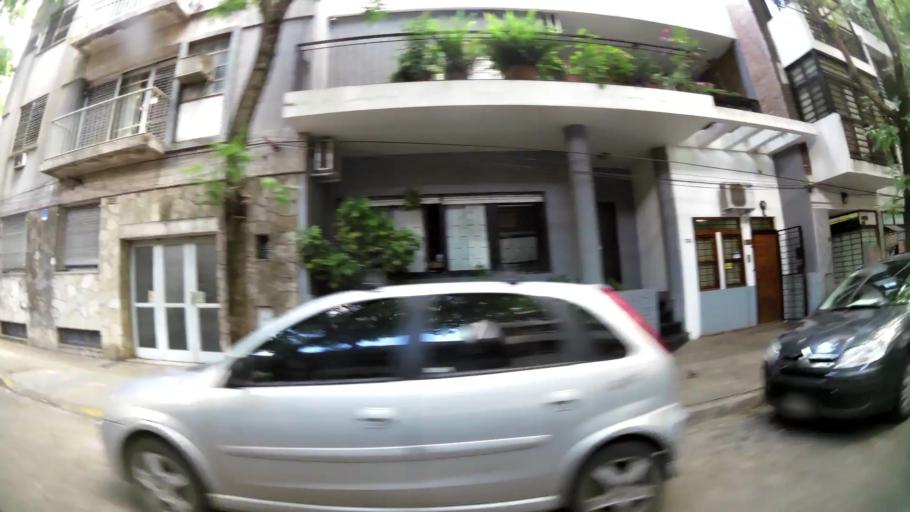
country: AR
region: Santa Fe
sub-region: Departamento de Rosario
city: Rosario
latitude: -32.9541
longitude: -60.6262
